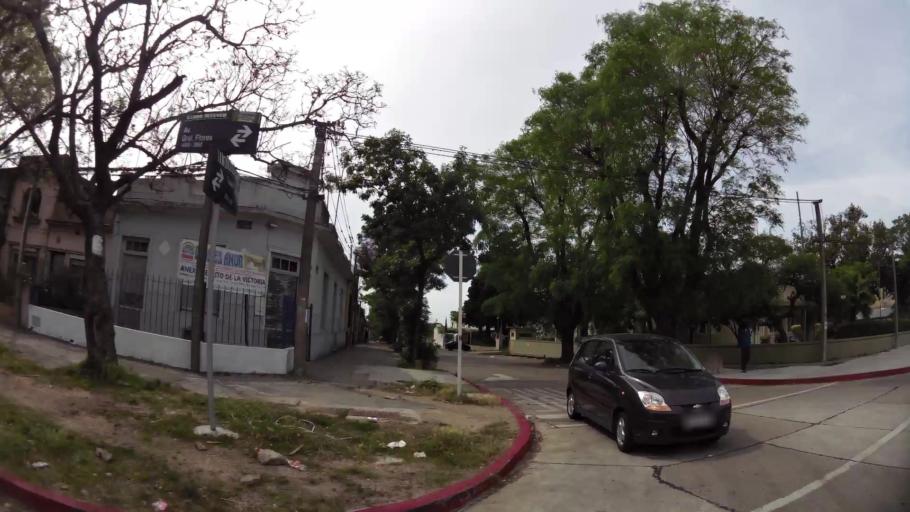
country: UY
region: Montevideo
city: Montevideo
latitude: -34.8567
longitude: -56.1638
